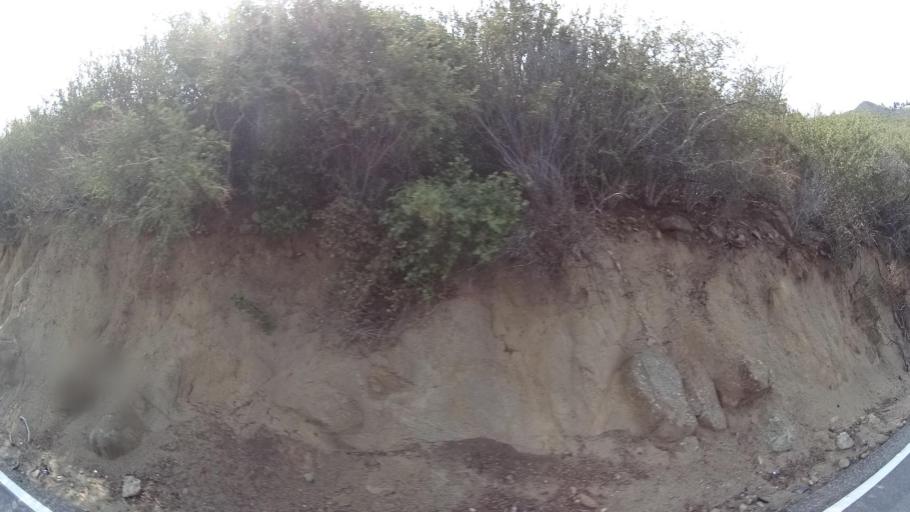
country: US
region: California
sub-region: San Diego County
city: Julian
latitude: 33.0750
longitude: -116.5608
